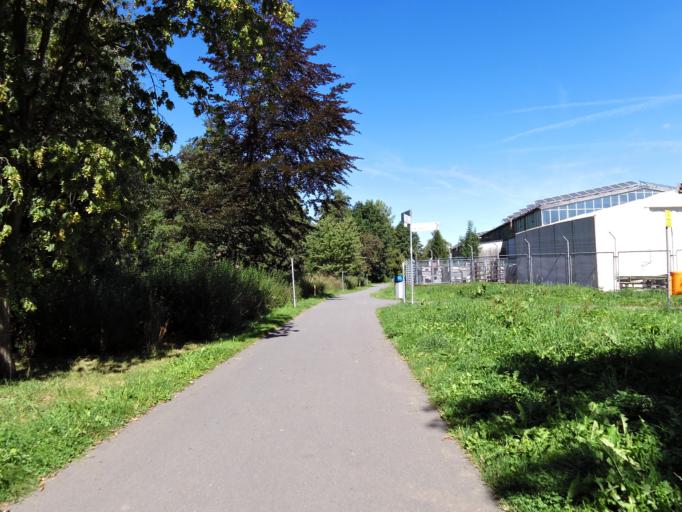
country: DE
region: Hesse
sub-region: Regierungsbezirk Darmstadt
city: Erbach
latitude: 49.6609
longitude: 8.9886
